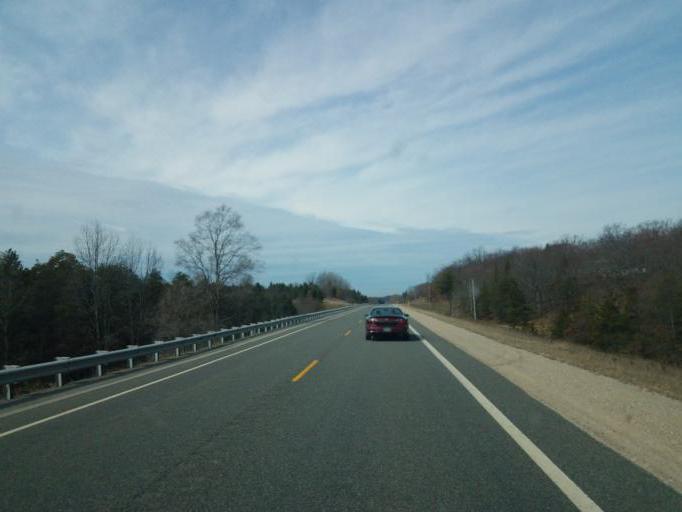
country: US
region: Michigan
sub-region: Oceana County
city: Shelby
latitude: 43.5714
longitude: -86.3175
